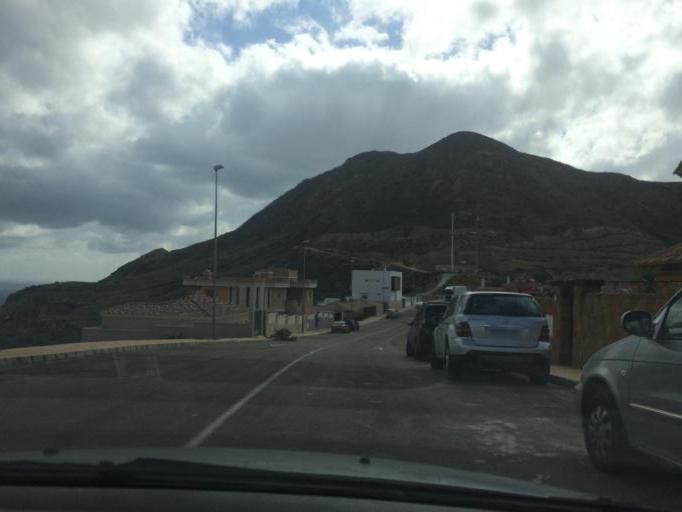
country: ES
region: Andalusia
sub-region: Provincia de Almeria
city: Vicar
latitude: 36.8332
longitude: -2.6121
